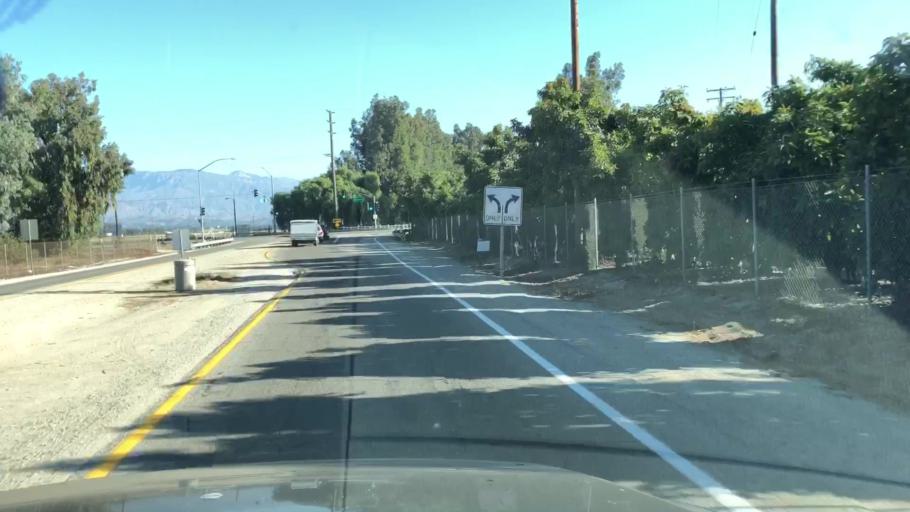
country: US
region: California
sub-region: Ventura County
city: Saticoy
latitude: 34.2670
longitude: -119.1269
